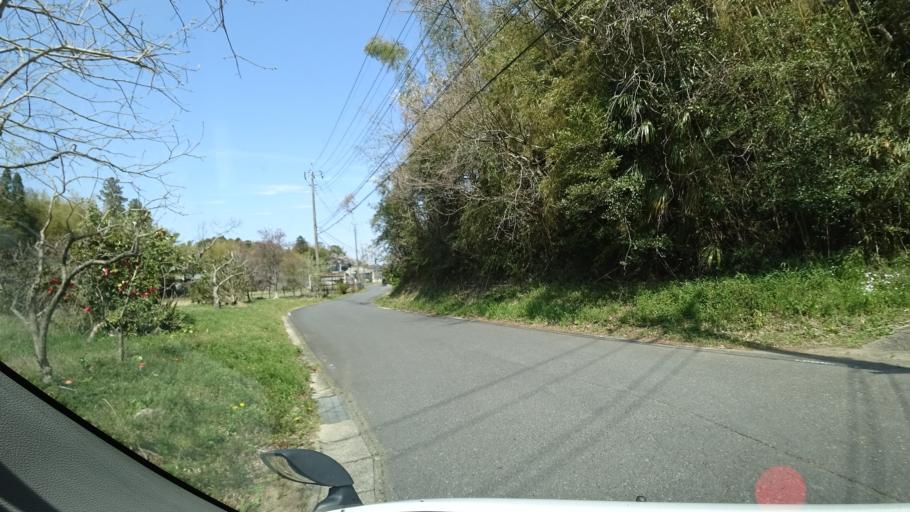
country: JP
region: Chiba
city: Narita
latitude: 35.7859
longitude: 140.3504
